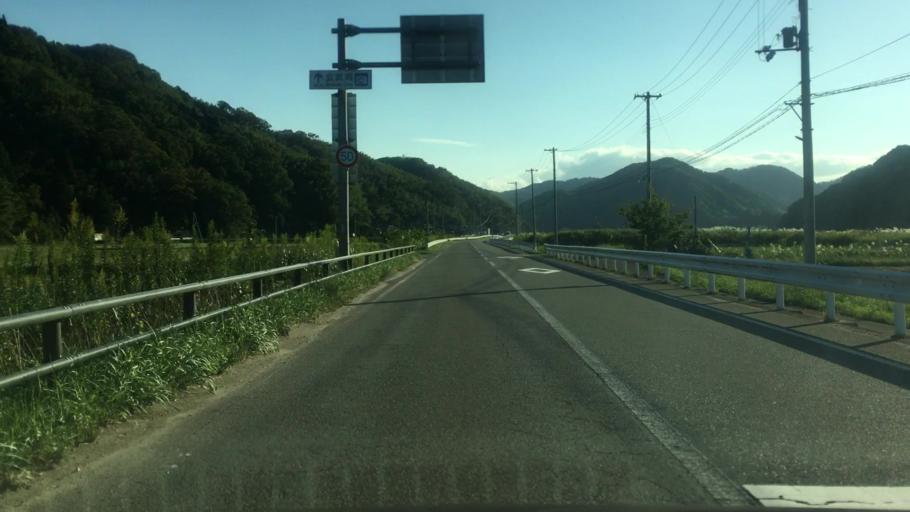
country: JP
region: Hyogo
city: Toyooka
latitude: 35.6178
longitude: 134.8144
